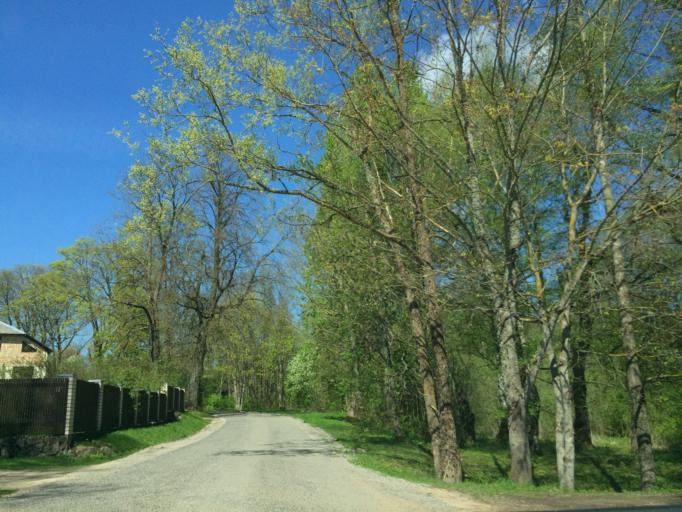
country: LV
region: Baldone
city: Baldone
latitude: 56.7396
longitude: 24.3746
